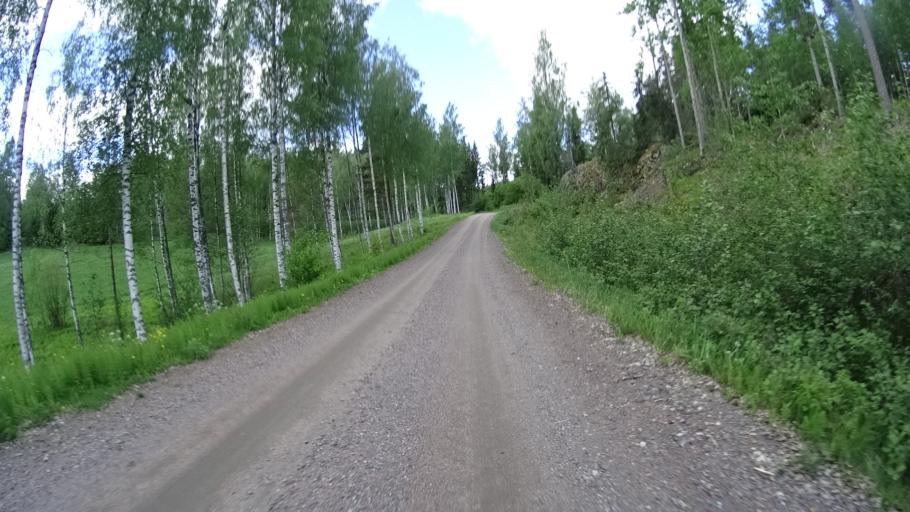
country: FI
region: Uusimaa
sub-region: Raaseporin
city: Karis
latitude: 60.1406
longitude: 23.6220
